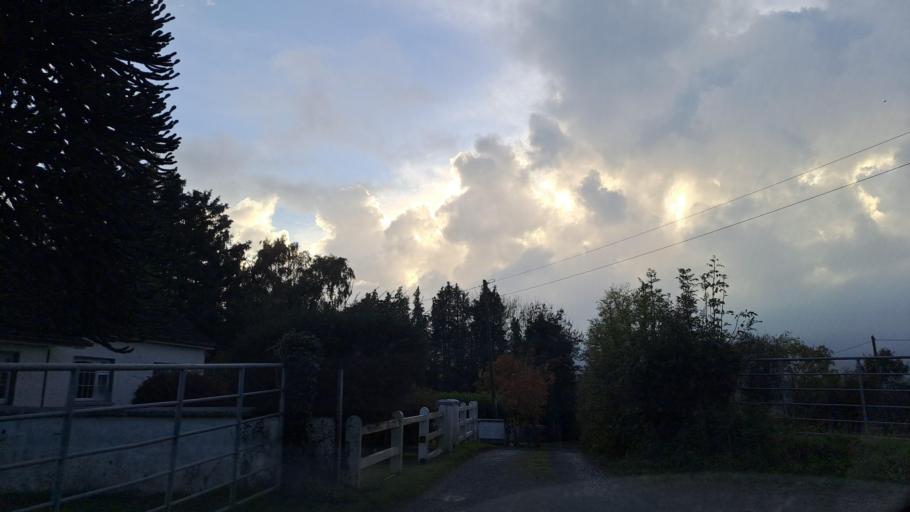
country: IE
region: Ulster
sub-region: County Monaghan
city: Carrickmacross
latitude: 53.9737
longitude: -6.7514
